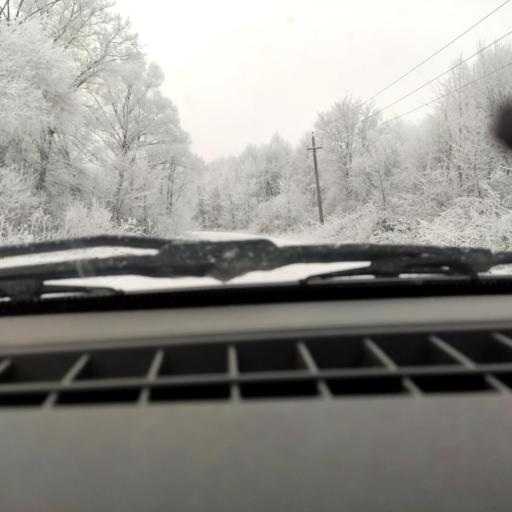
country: RU
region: Bashkortostan
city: Ufa
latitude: 54.7162
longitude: 56.1306
